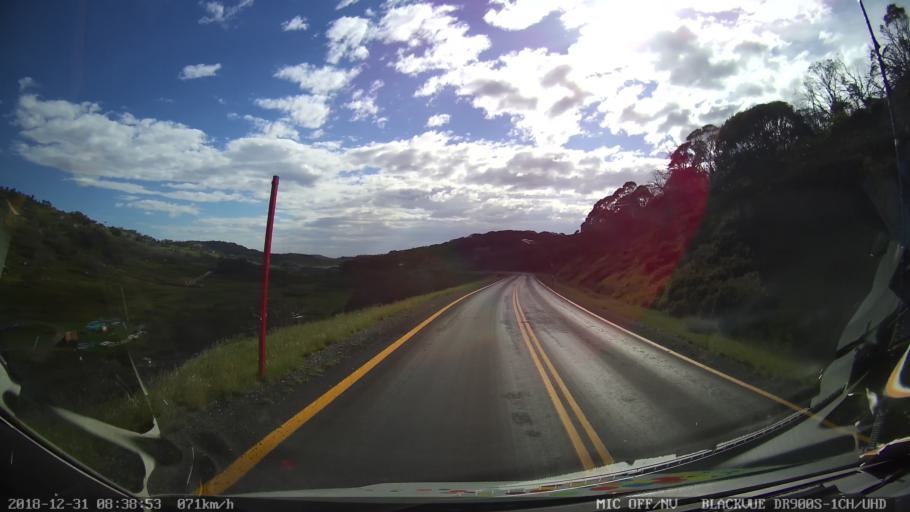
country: AU
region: New South Wales
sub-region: Snowy River
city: Jindabyne
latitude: -36.4116
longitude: 148.4001
